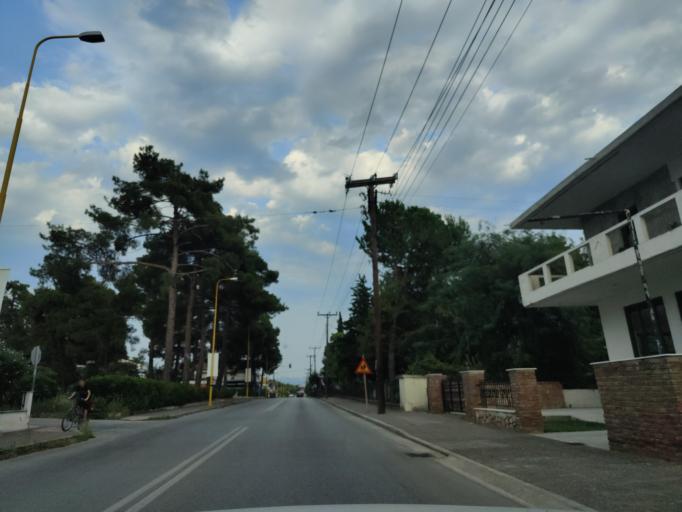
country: GR
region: East Macedonia and Thrace
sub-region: Nomos Dramas
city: Drama
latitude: 41.1534
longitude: 24.1216
